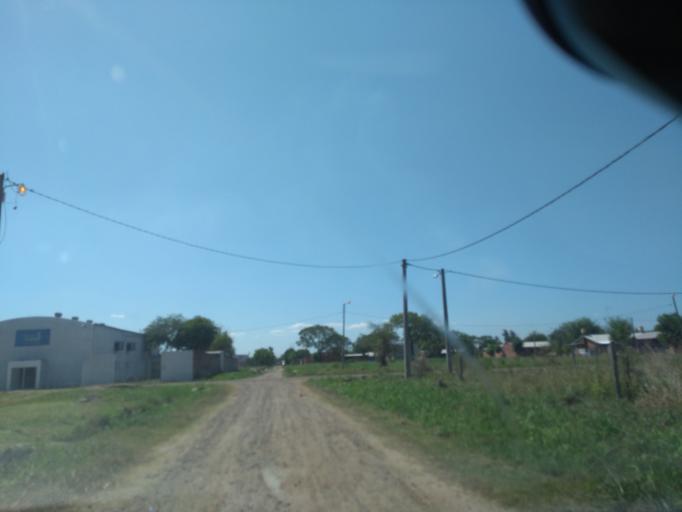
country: AR
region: Chaco
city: Fontana
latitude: -27.4146
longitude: -59.0376
